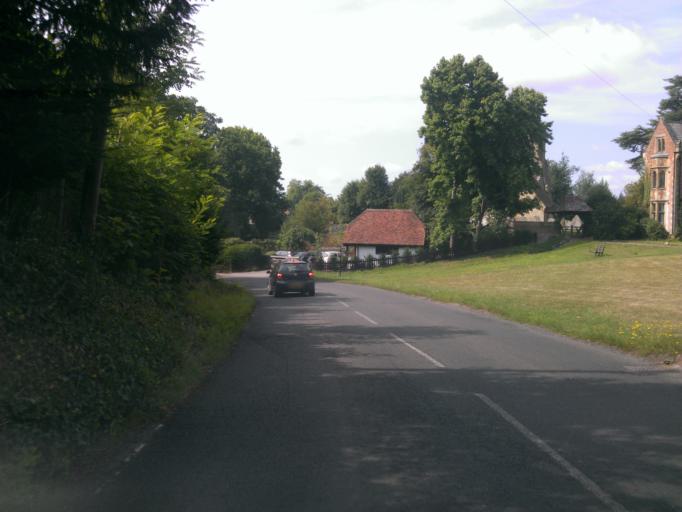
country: GB
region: England
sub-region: Kent
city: Tonbridge
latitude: 51.1984
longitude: 0.2168
